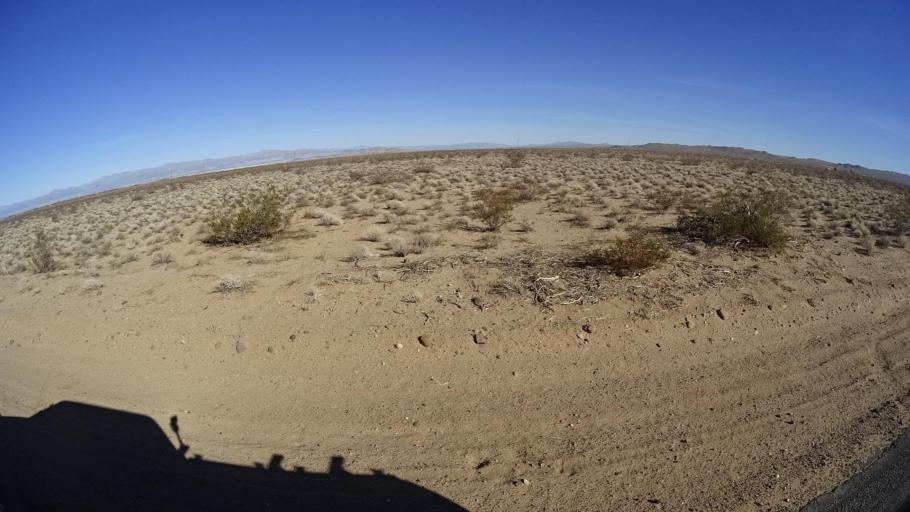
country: US
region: California
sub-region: Kern County
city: China Lake Acres
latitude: 35.5783
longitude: -117.7857
